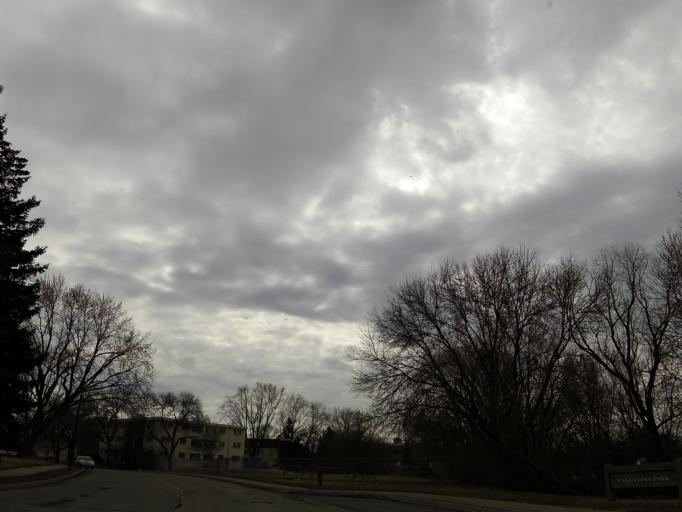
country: US
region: Minnesota
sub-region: Hennepin County
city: Edina
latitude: 44.8675
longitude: -93.3373
